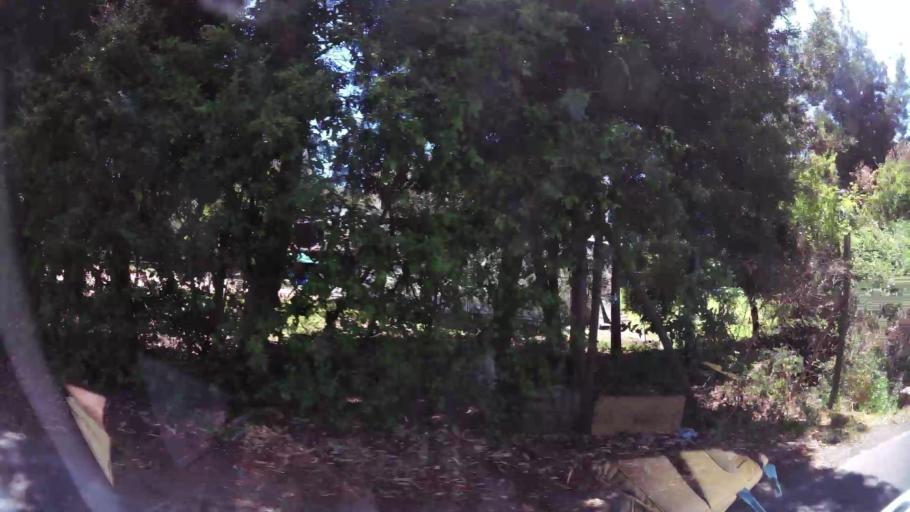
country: CL
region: Maule
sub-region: Provincia de Curico
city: Curico
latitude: -34.9985
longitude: -71.2090
